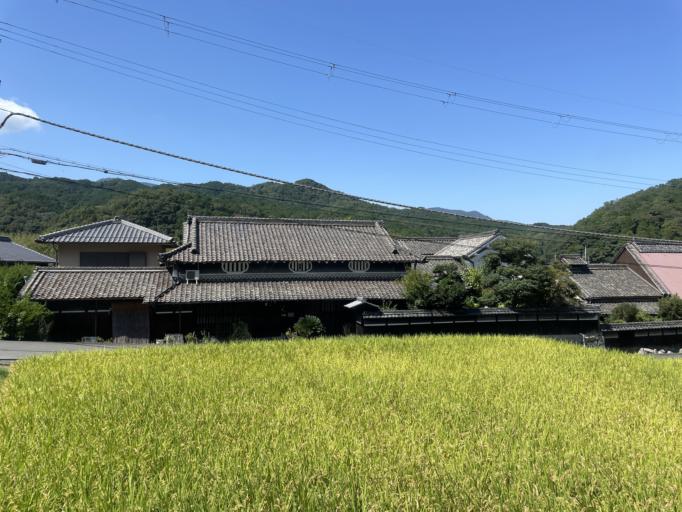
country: JP
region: Nara
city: Gose
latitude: 34.4116
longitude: 135.7464
